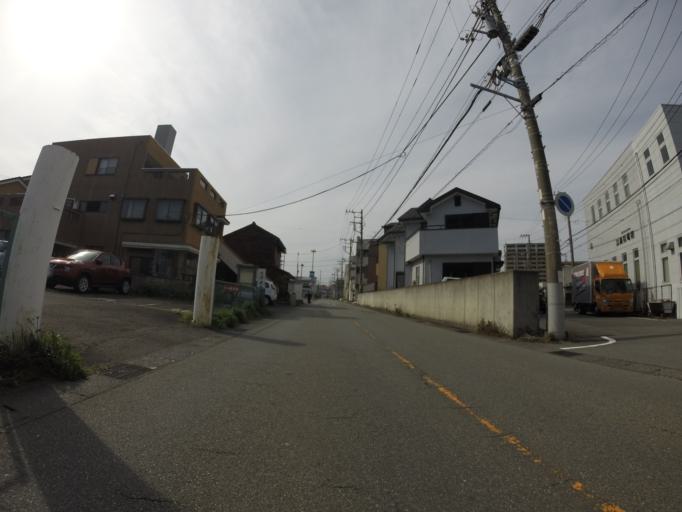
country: JP
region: Shizuoka
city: Numazu
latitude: 35.0883
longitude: 138.8664
